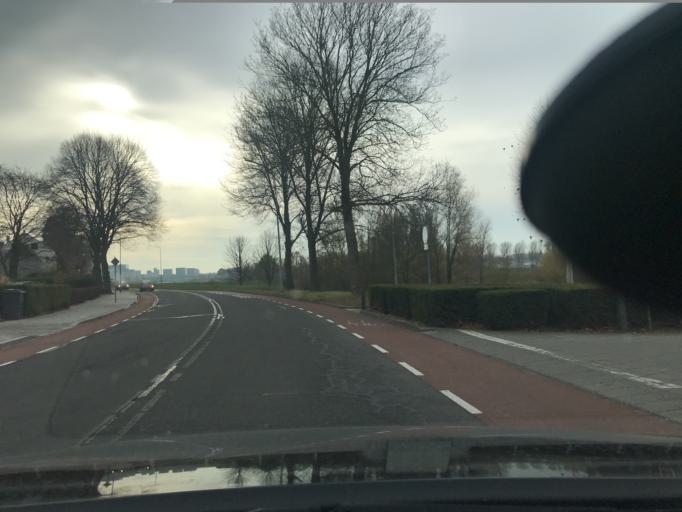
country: NL
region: Limburg
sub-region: Gemeente Venlo
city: Venlo
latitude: 51.3826
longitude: 6.1675
